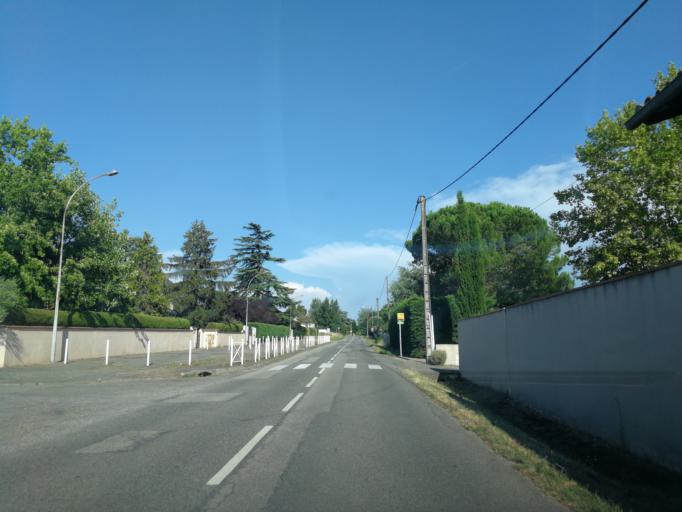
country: FR
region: Midi-Pyrenees
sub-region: Departement de la Haute-Garonne
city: Balma
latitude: 43.6211
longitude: 1.5088
